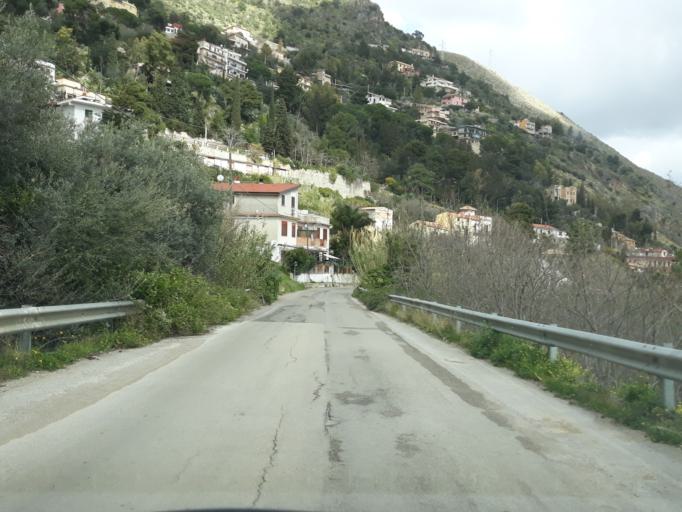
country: IT
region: Sicily
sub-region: Palermo
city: Monreale
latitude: 38.0856
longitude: 13.2979
